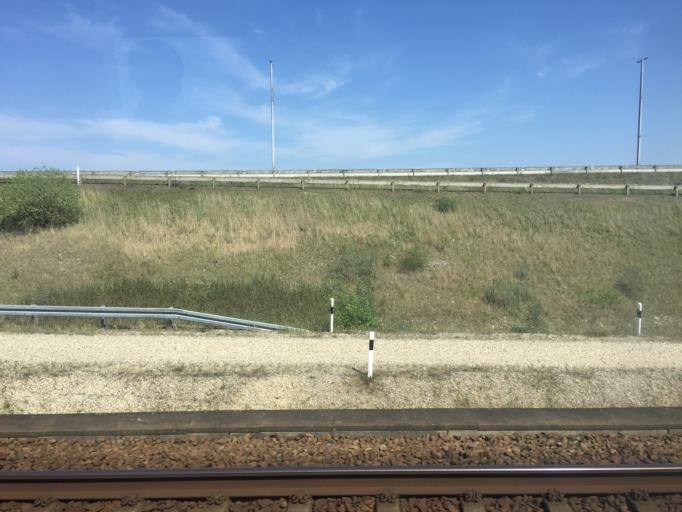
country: DK
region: Capital Region
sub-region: Dragor Kommune
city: Dragor
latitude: 55.6019
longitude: 12.7459
